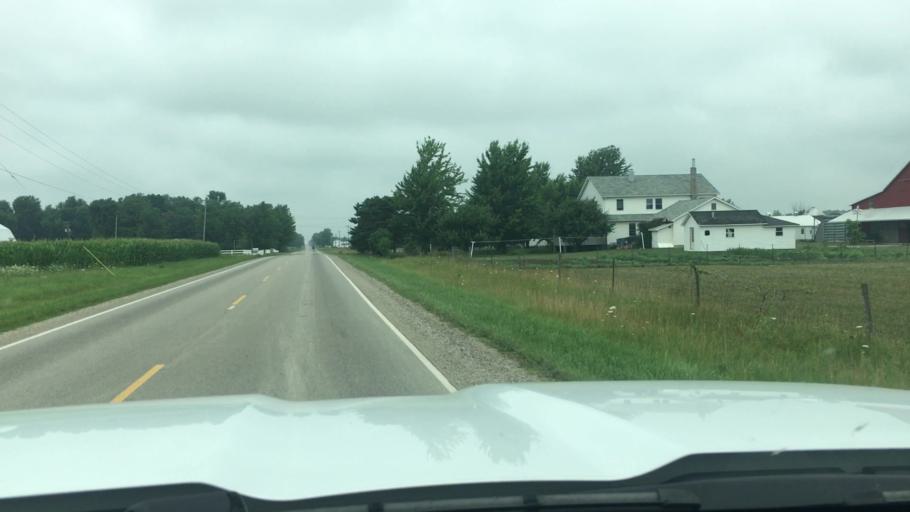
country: US
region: Michigan
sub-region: Sanilac County
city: Brown City
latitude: 43.2935
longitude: -82.9831
